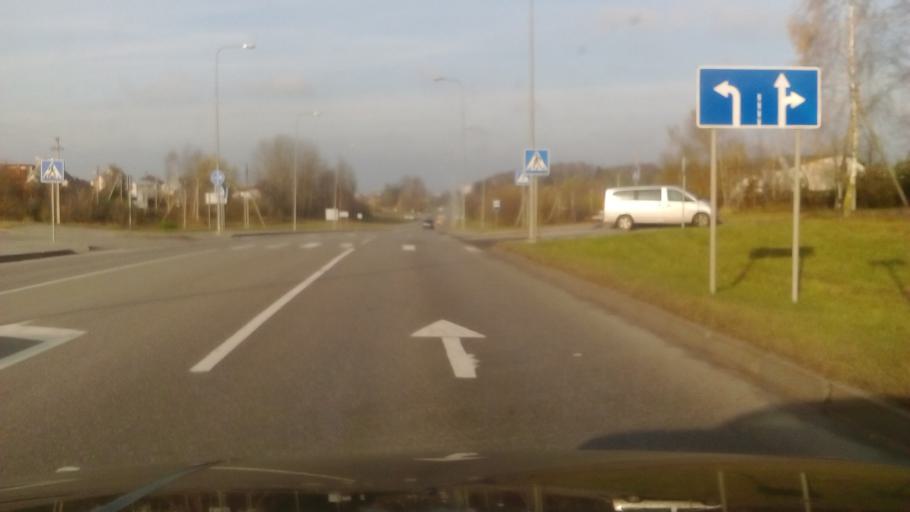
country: LT
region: Alytaus apskritis
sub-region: Alytus
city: Alytus
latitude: 54.3966
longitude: 23.9996
